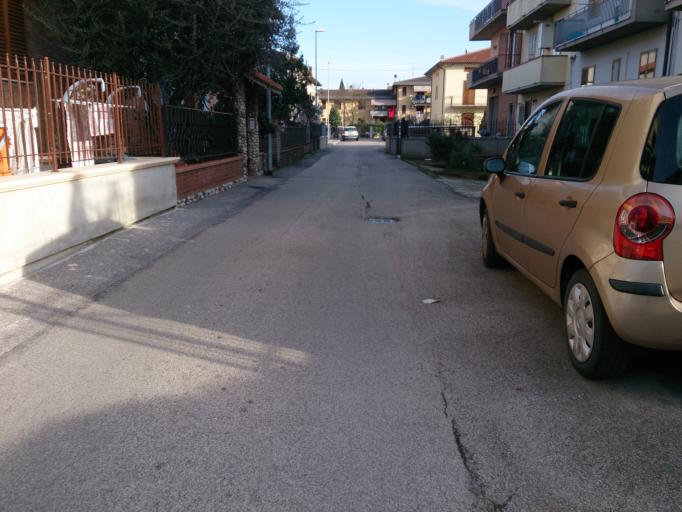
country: IT
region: Tuscany
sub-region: Provincia di Prato
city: Fornacelle
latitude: 43.8916
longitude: 11.0482
